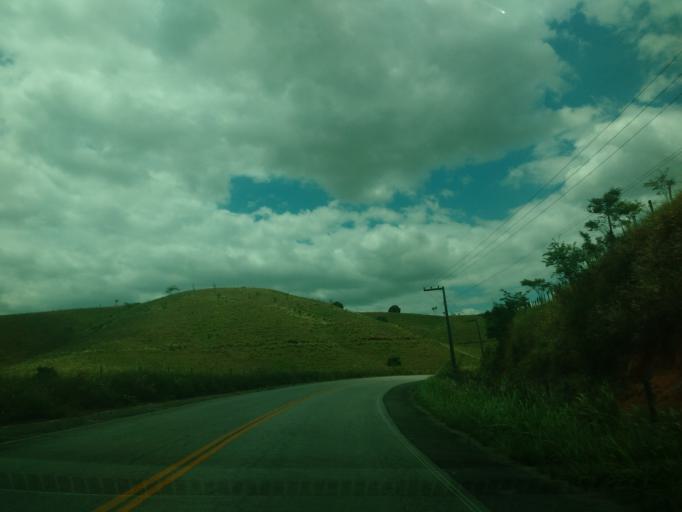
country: BR
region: Alagoas
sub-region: Uniao Dos Palmares
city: Uniao dos Palmares
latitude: -9.1376
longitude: -36.1194
